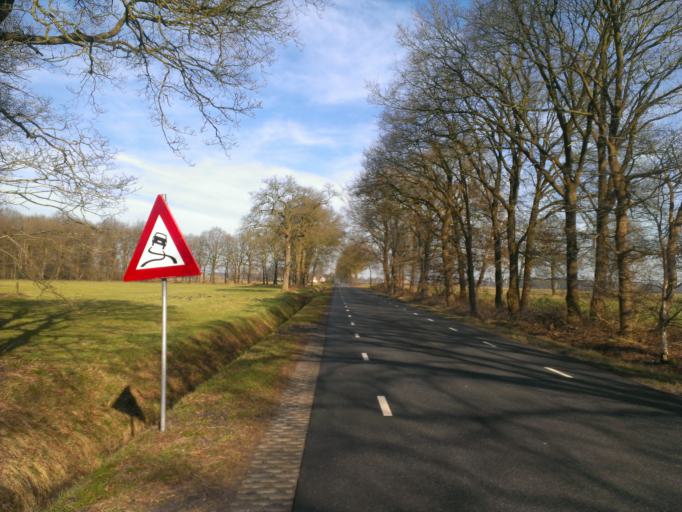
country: NL
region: Drenthe
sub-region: Gemeente Hoogeveen
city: Hoogeveen
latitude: 52.7444
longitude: 6.4765
